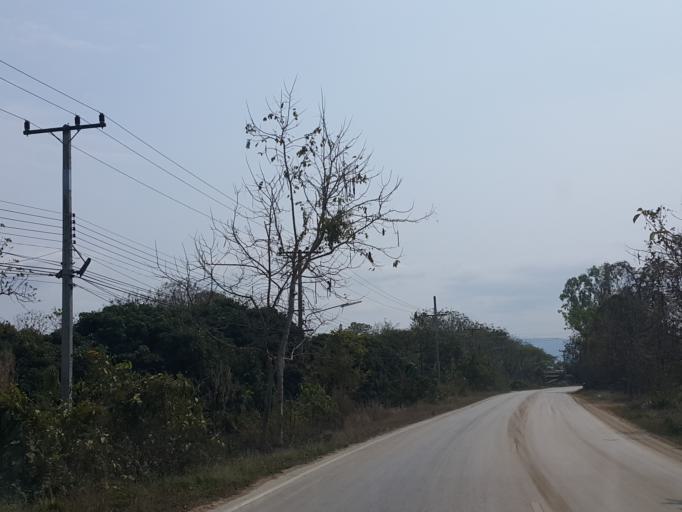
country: TH
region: Lamphun
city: Ban Thi
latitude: 18.6637
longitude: 99.1031
